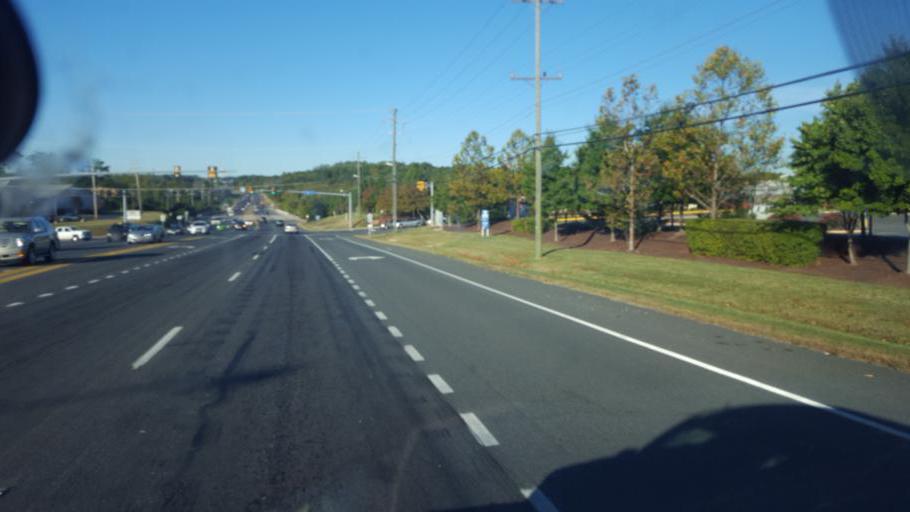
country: US
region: Virginia
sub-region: Prince William County
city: Bull Run
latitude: 38.7379
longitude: -77.5319
